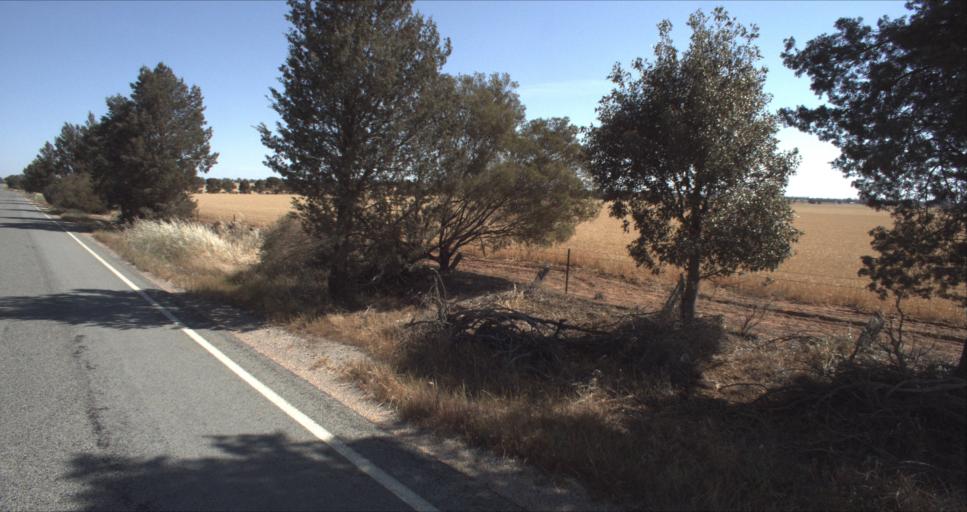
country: AU
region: New South Wales
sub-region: Leeton
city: Leeton
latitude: -34.4659
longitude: 146.4368
